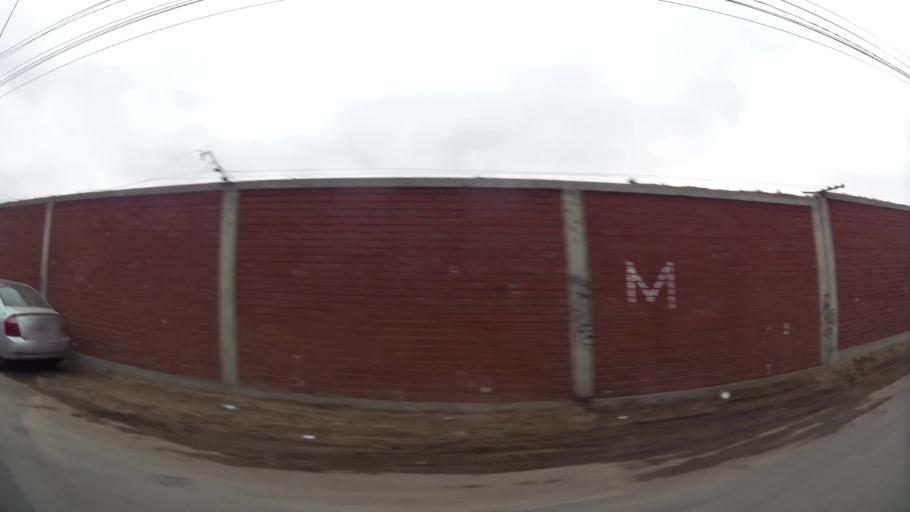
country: PE
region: Lima
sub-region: Lima
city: Vitarte
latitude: -12.0443
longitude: -76.9515
